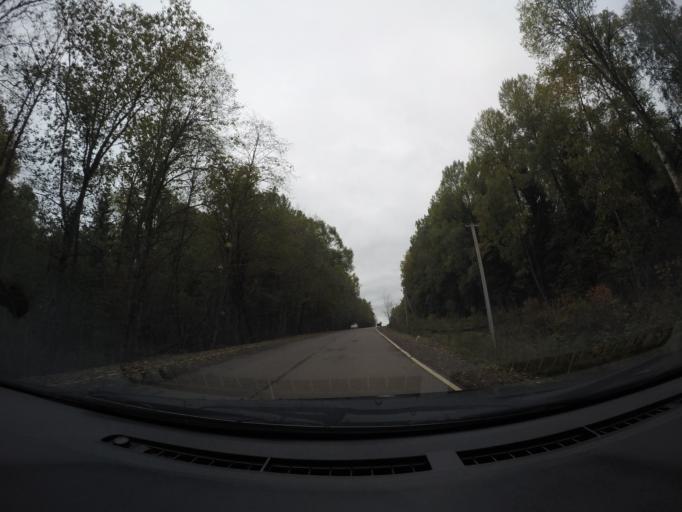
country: RU
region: Moskovskaya
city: Ruza
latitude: 55.7890
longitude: 36.2494
